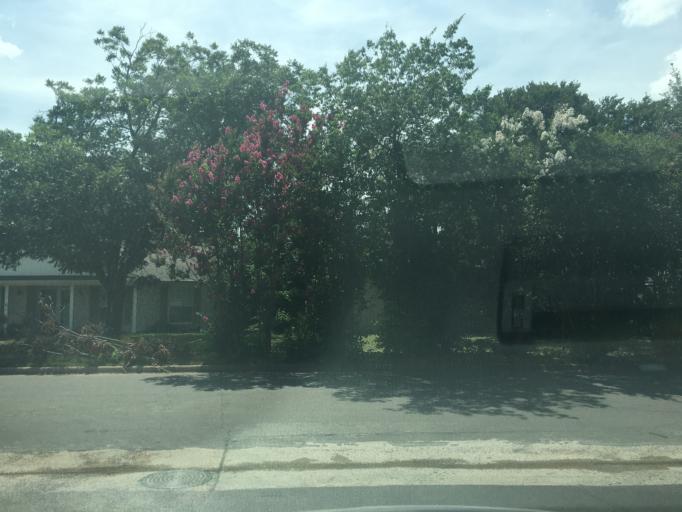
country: US
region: Texas
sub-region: Dallas County
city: Farmers Branch
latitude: 32.9154
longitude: -96.8513
